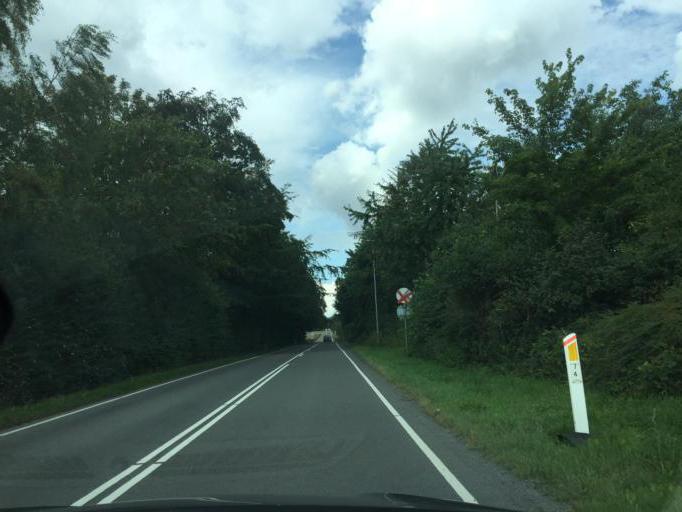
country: DK
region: South Denmark
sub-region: Odense Kommune
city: Stige
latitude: 55.4534
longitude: 10.3697
